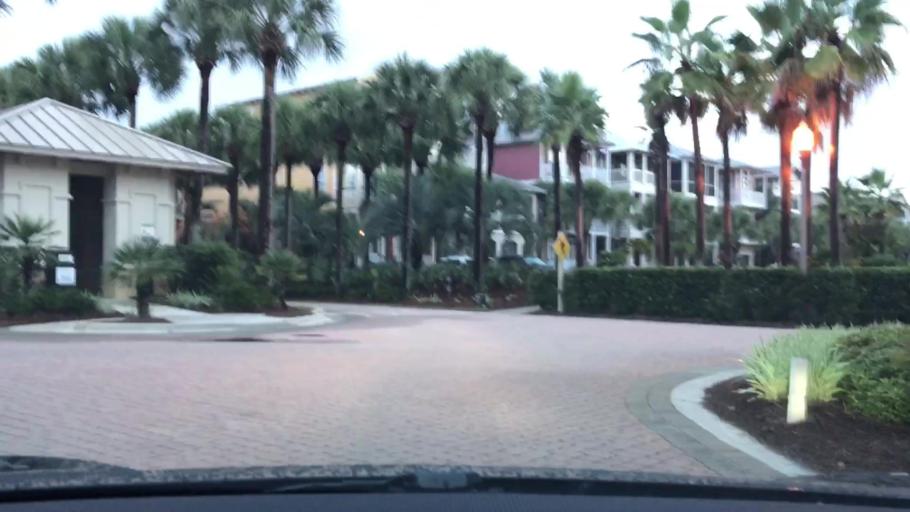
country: US
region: Florida
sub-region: Bay County
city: Laguna Beach
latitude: 30.2828
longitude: -86.0216
